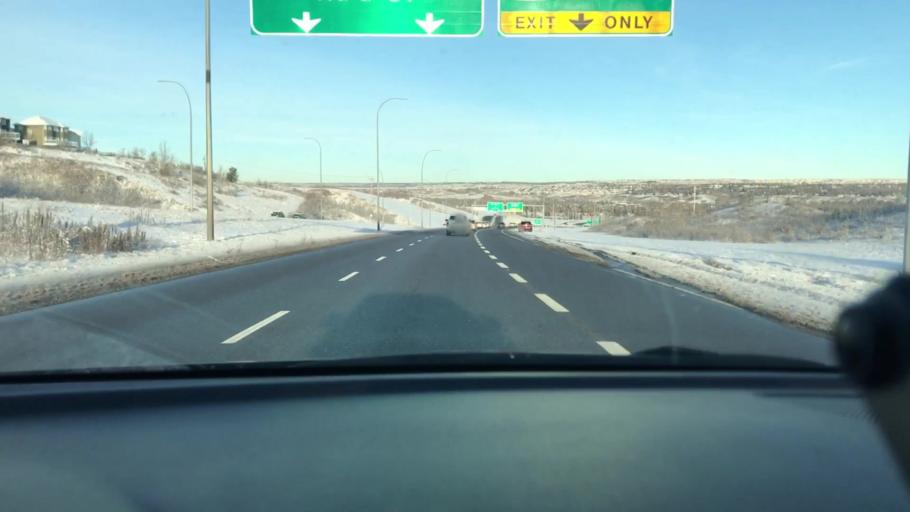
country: CA
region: Alberta
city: Calgary
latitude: 51.0724
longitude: -114.1835
